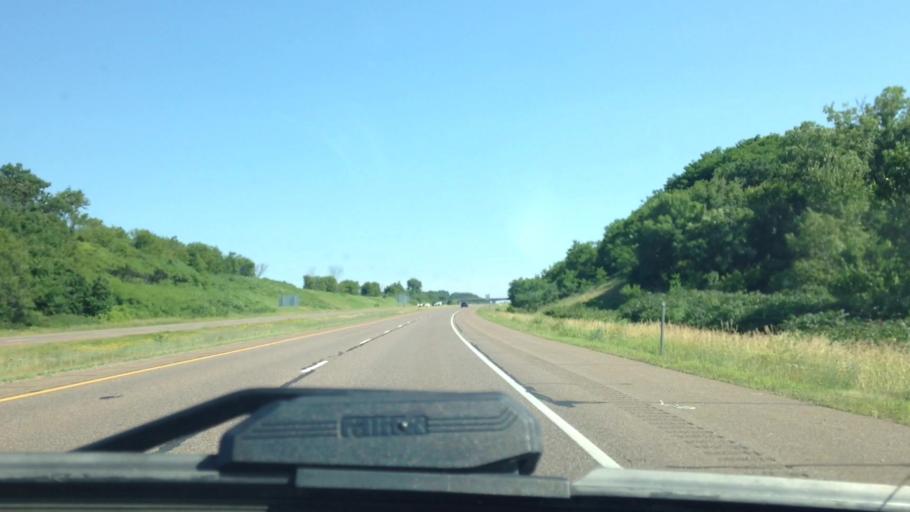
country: US
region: Wisconsin
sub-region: Chippewa County
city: Chippewa Falls
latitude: 44.9313
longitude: -91.4282
